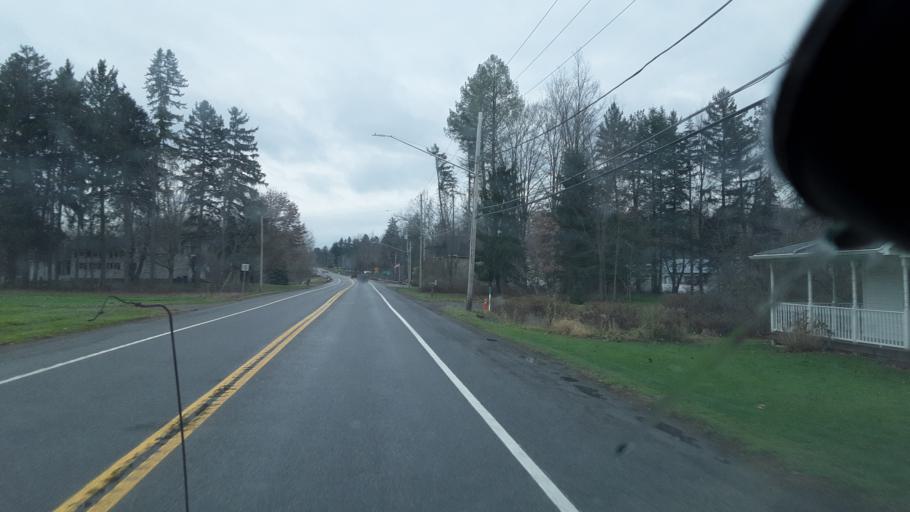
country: US
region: New York
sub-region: Erie County
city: Holland
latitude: 42.6775
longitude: -78.5622
